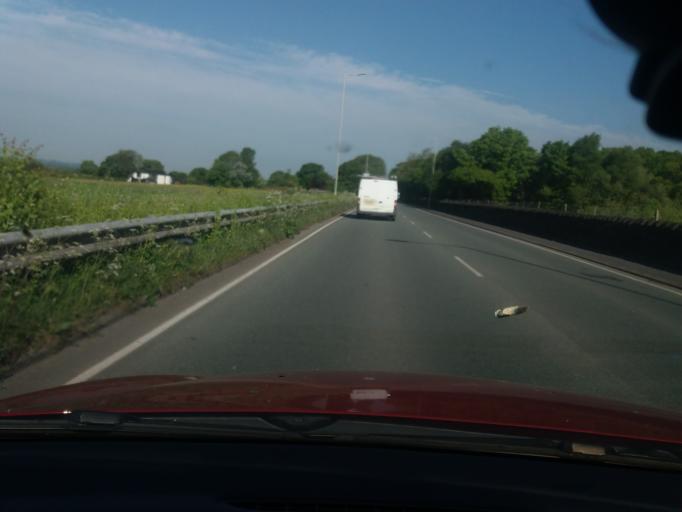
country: GB
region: England
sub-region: Borough of Wigan
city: Haigh
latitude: 53.6089
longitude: -2.5710
